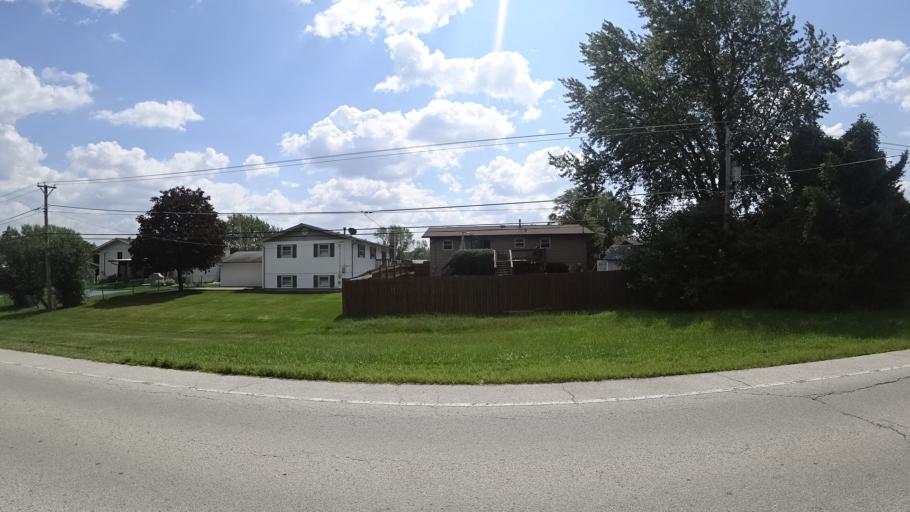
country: US
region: Illinois
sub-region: Cook County
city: Oak Forest
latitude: 41.6173
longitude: -87.7710
